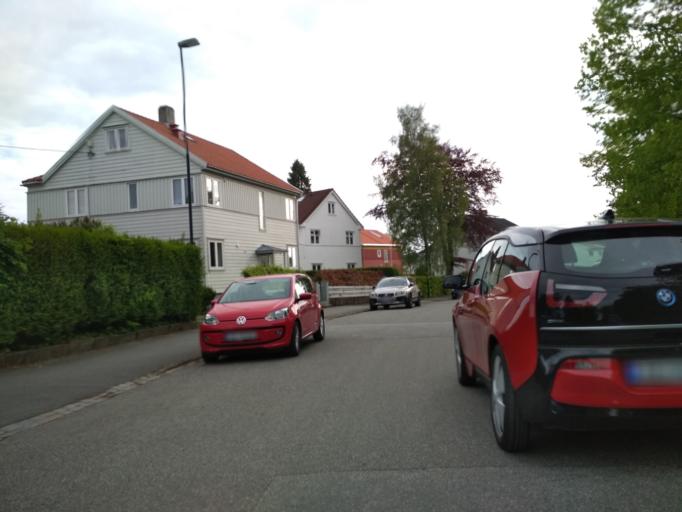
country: NO
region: Rogaland
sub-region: Stavanger
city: Stavanger
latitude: 58.9664
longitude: 5.7173
